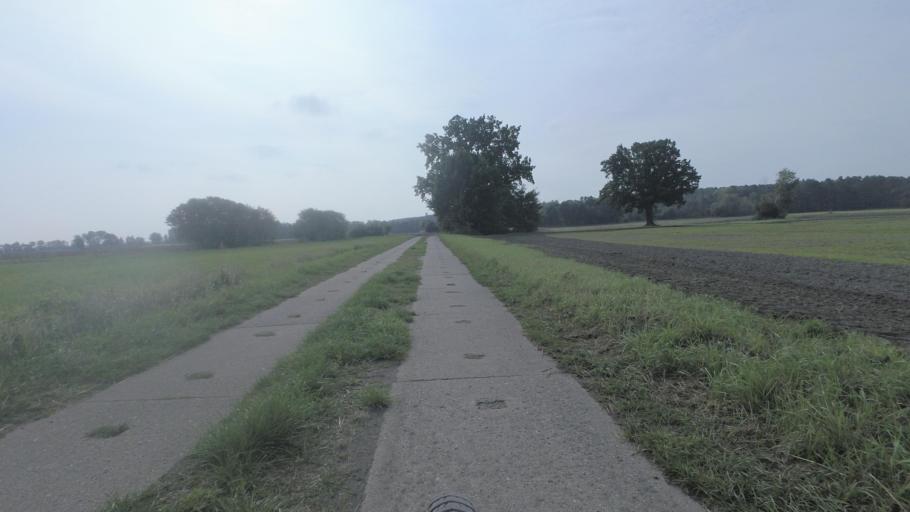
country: DE
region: Brandenburg
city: Rangsdorf
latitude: 52.2733
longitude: 13.3898
